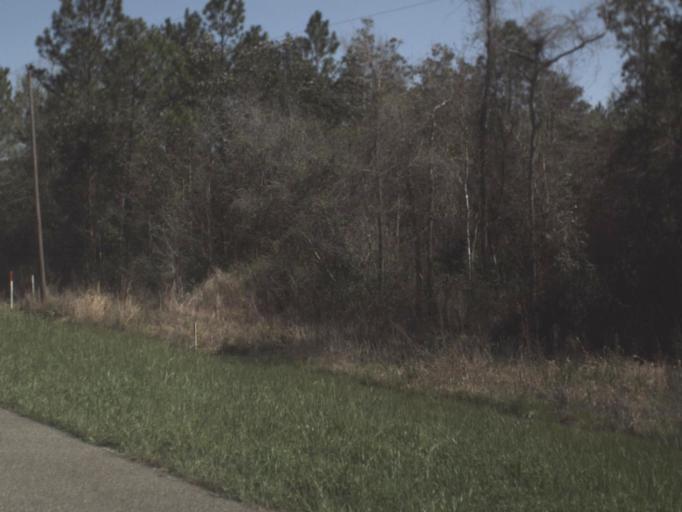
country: US
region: Florida
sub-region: Calhoun County
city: Blountstown
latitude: 30.4291
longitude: -85.1078
